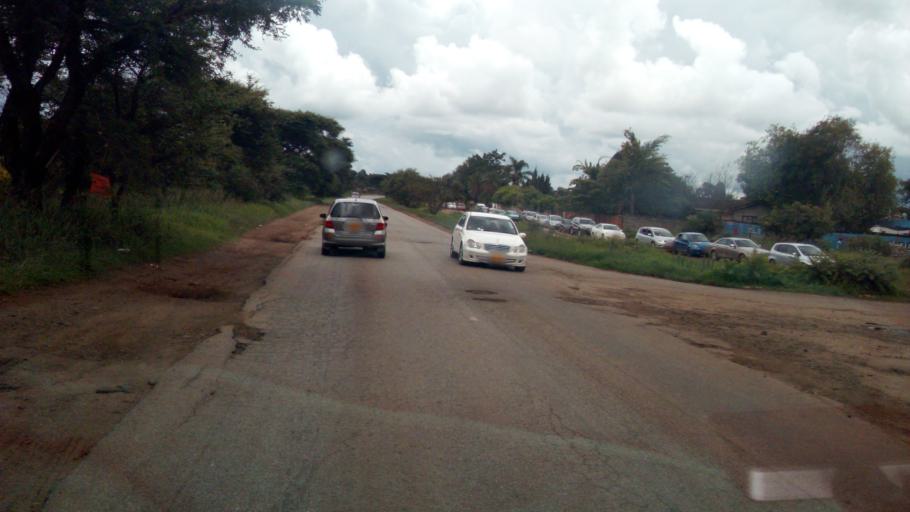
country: ZW
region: Harare
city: Harare
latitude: -17.7761
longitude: 30.9953
